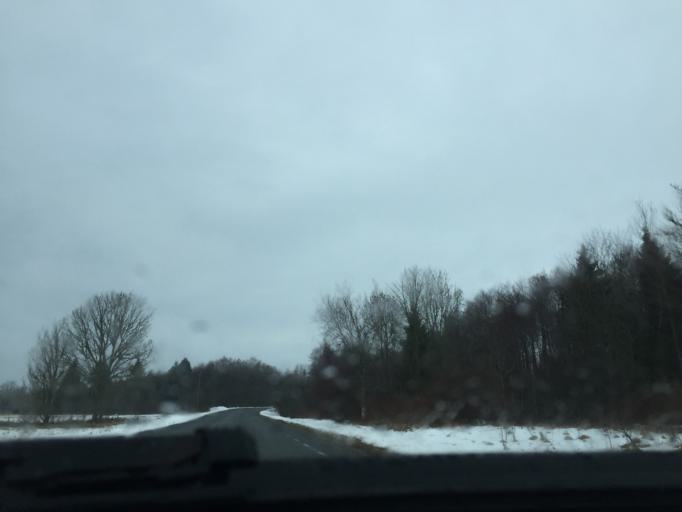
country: EE
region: Saare
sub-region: Kuressaare linn
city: Kuressaare
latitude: 58.3200
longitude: 22.0226
